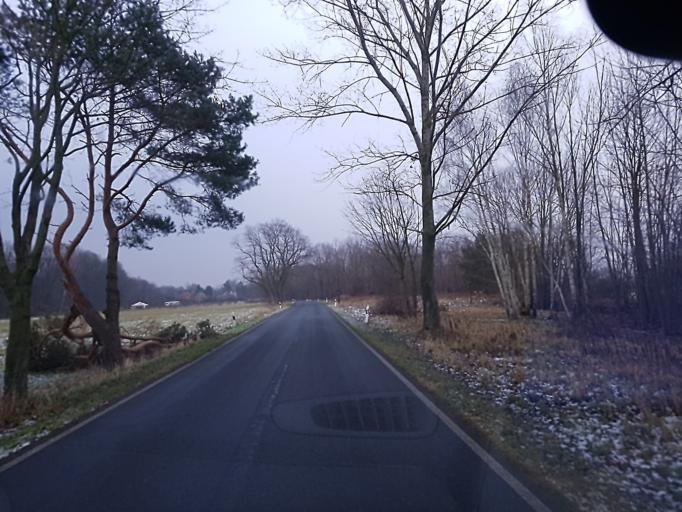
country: DE
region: Brandenburg
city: Lubbenau
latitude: 51.8245
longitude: 13.9150
